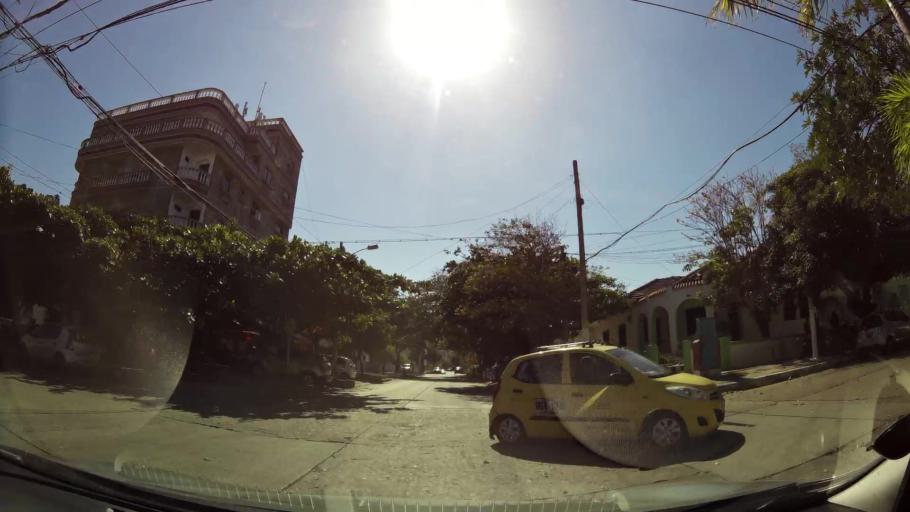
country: CO
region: Atlantico
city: Barranquilla
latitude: 11.0000
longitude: -74.7942
